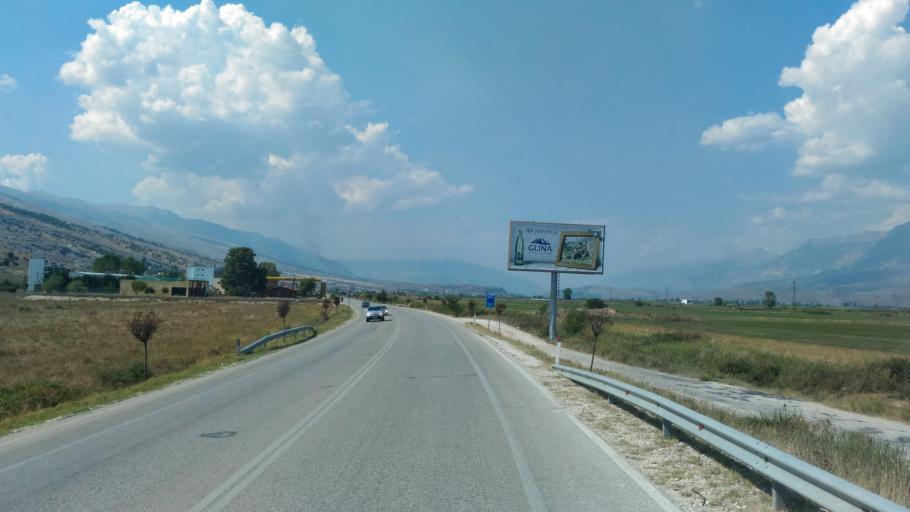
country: AL
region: Gjirokaster
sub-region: Rrethi i Gjirokastres
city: Dervician
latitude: 40.0049
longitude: 20.2097
